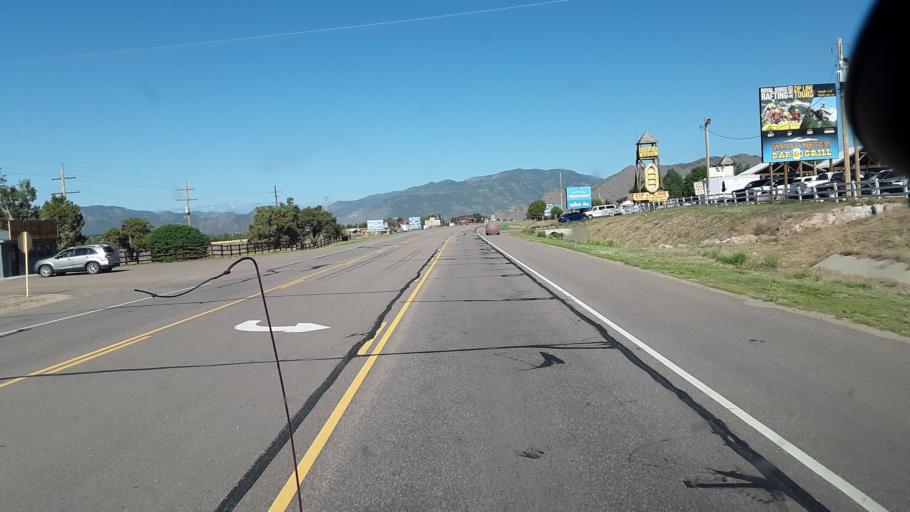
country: US
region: Colorado
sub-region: Fremont County
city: Canon City
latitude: 38.4957
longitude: -105.3157
